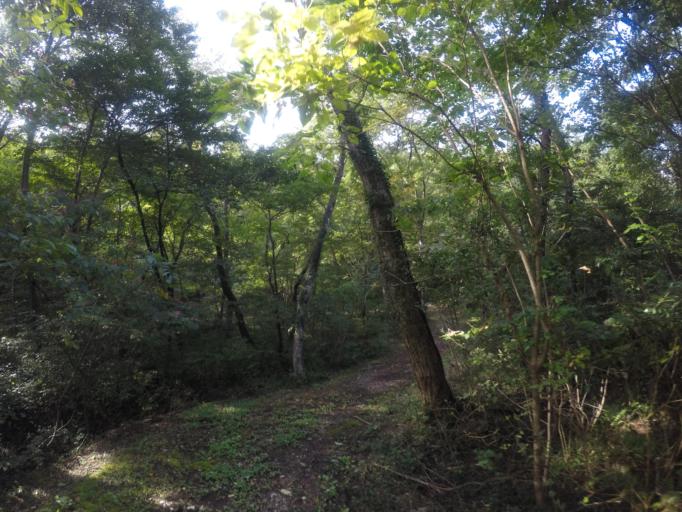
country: JP
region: Fukushima
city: Fukushima-shi
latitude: 37.7058
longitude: 140.3498
